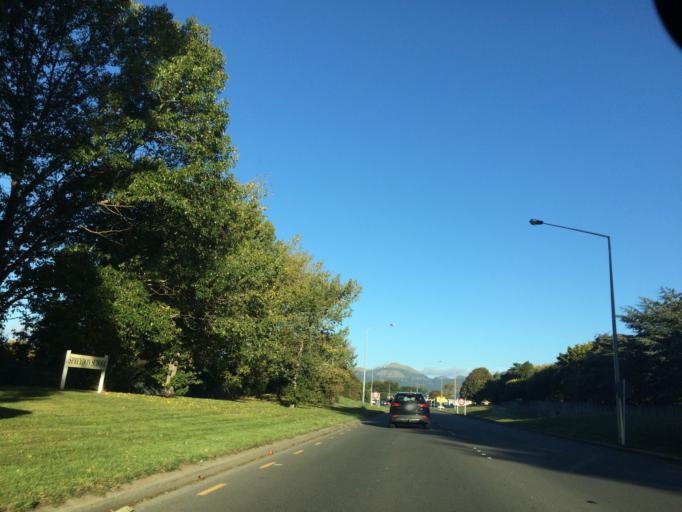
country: NZ
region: Canterbury
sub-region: Christchurch City
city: Christchurch
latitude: -43.5530
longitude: 172.5906
